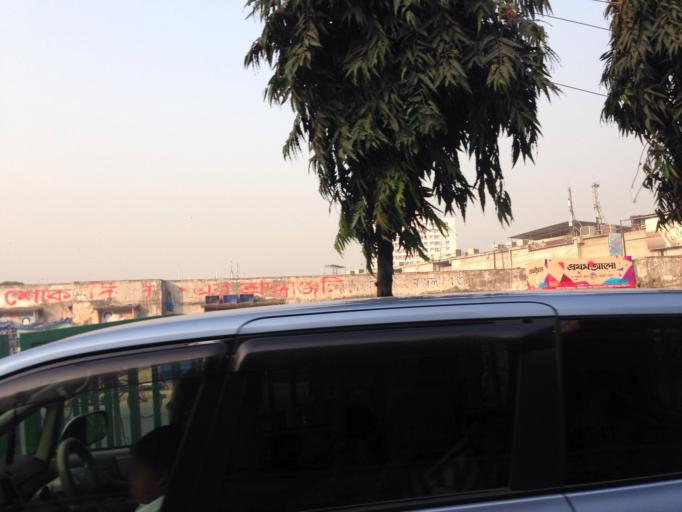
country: BD
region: Dhaka
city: Azimpur
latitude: 23.7339
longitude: 90.3845
